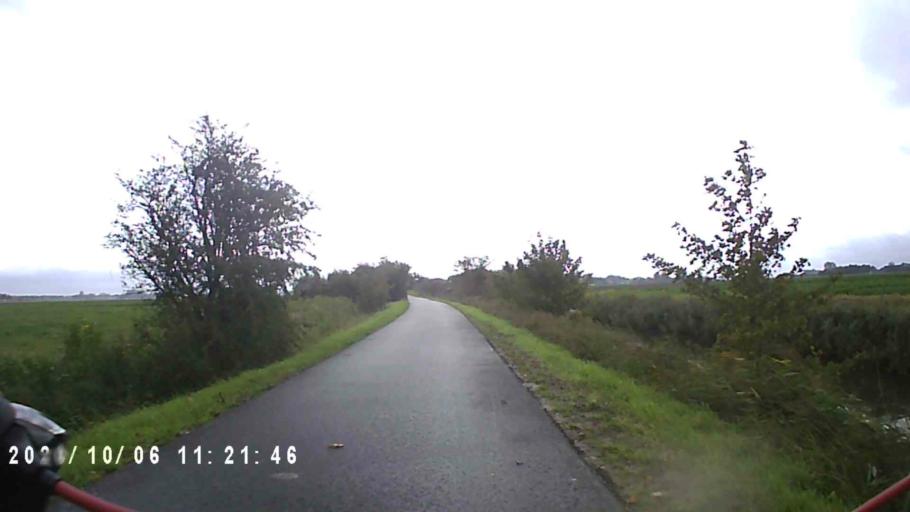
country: NL
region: Groningen
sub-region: Gemeente Zuidhorn
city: Oldehove
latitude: 53.3467
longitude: 6.4085
